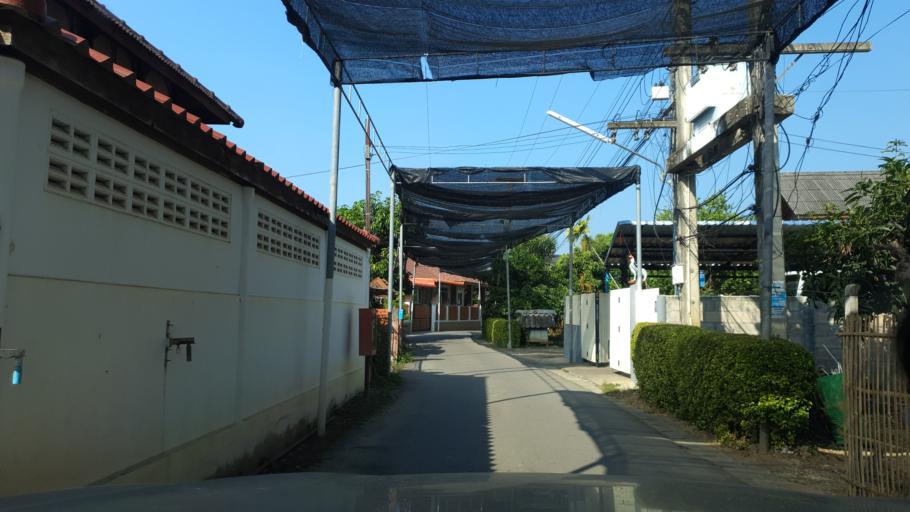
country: TH
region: Chiang Mai
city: Hang Dong
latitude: 18.7253
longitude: 98.9422
